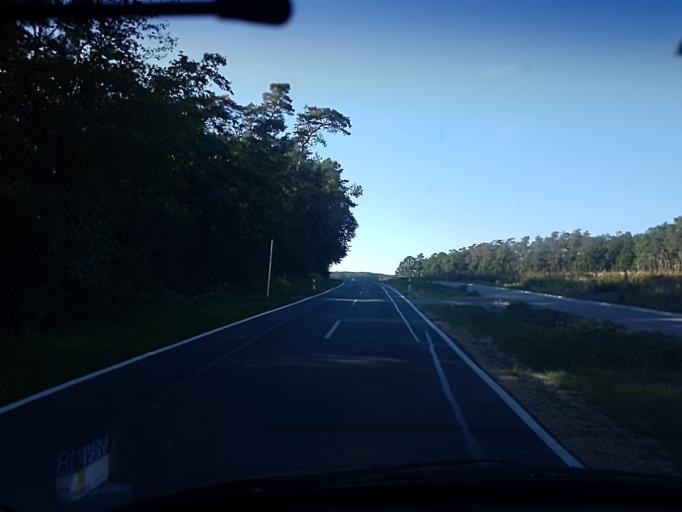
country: DE
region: Bavaria
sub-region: Upper Franconia
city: Hallerndorf
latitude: 49.7484
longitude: 10.9571
